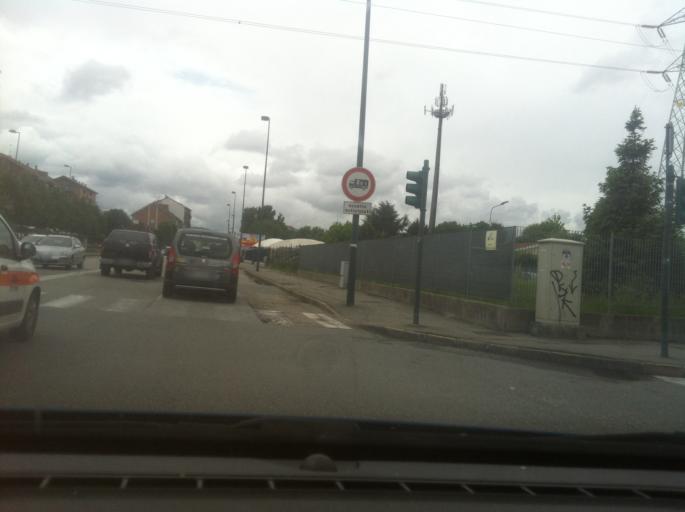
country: IT
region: Piedmont
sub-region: Provincia di Torino
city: San Mauro Torinese
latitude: 45.1077
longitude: 7.7280
